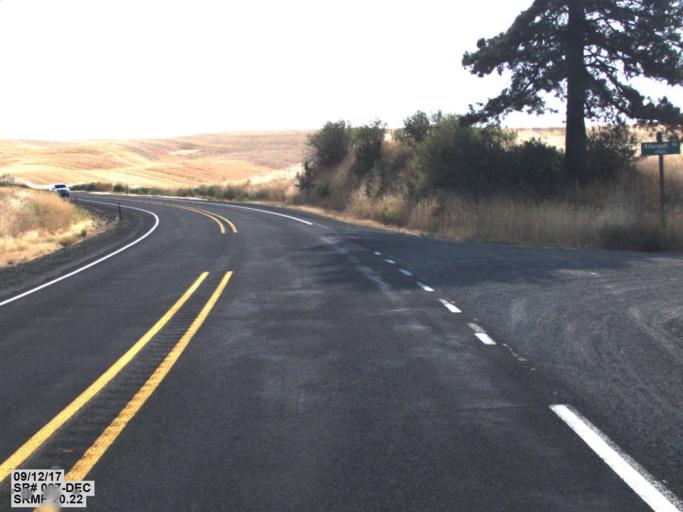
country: US
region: Washington
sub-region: Whitman County
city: Pullman
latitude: 46.9622
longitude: -117.1064
